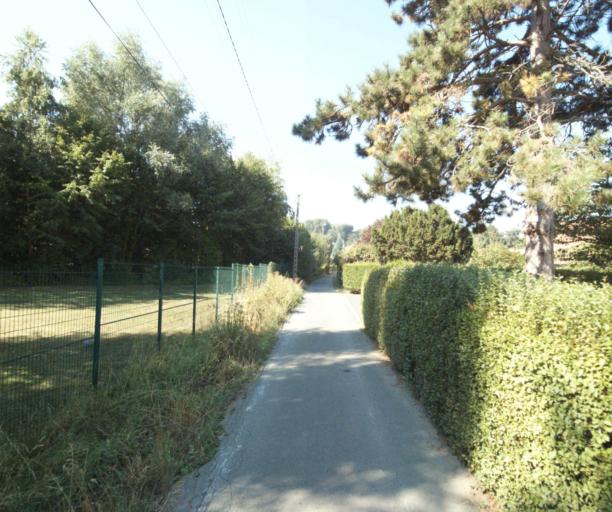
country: FR
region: Nord-Pas-de-Calais
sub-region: Departement du Nord
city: Wervicq-Sud
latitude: 50.7672
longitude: 3.0547
